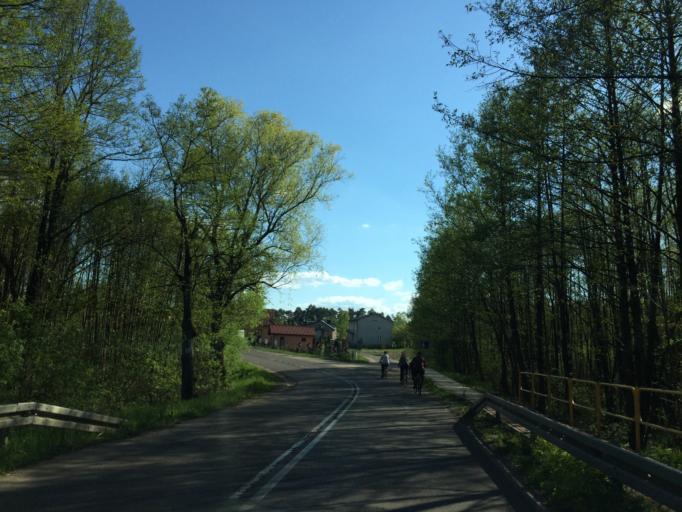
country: PL
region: Warmian-Masurian Voivodeship
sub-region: Powiat dzialdowski
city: Rybno
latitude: 53.3751
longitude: 19.9345
